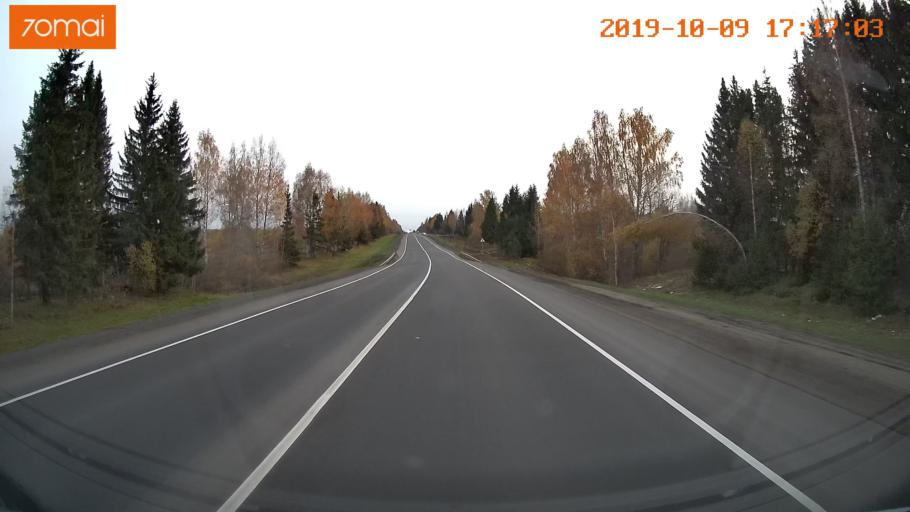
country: RU
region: Ivanovo
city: Furmanov
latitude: 57.2812
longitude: 41.1591
